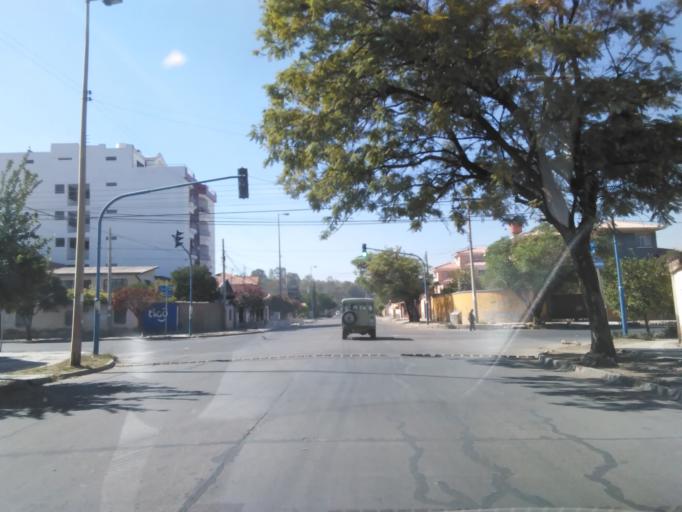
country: BO
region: Cochabamba
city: Cochabamba
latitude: -17.4001
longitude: -66.1795
